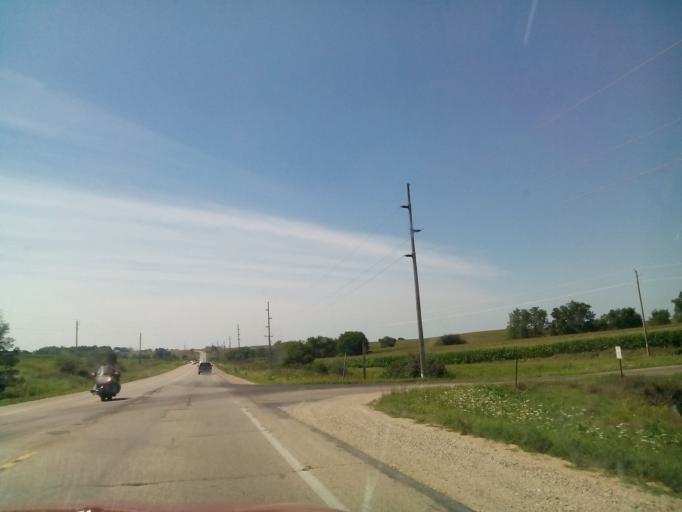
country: US
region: Wisconsin
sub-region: Green County
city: Monroe
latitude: 42.6668
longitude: -89.6209
